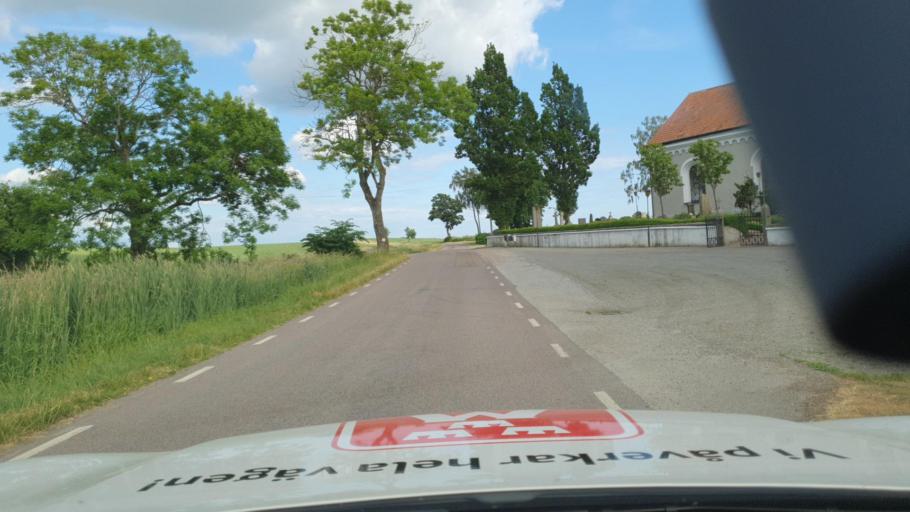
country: SE
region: Skane
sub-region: Skurups Kommun
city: Rydsgard
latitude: 55.4517
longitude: 13.5742
